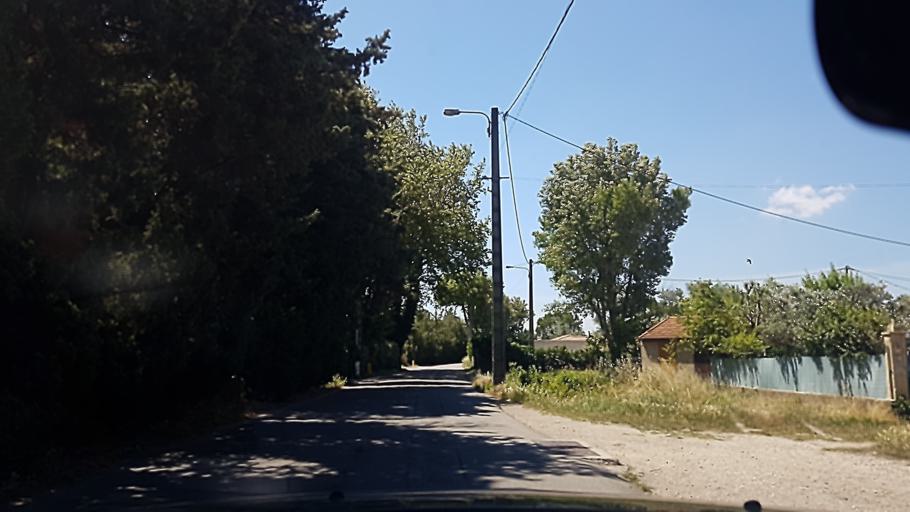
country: FR
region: Provence-Alpes-Cote d'Azur
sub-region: Departement du Vaucluse
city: Sorgues
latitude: 43.9878
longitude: 4.8761
